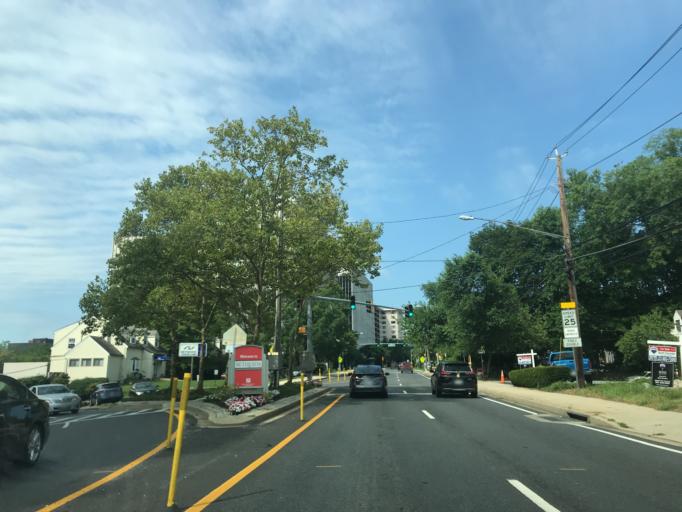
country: US
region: Maryland
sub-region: Montgomery County
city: Bethesda
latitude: 38.9860
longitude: -77.0864
